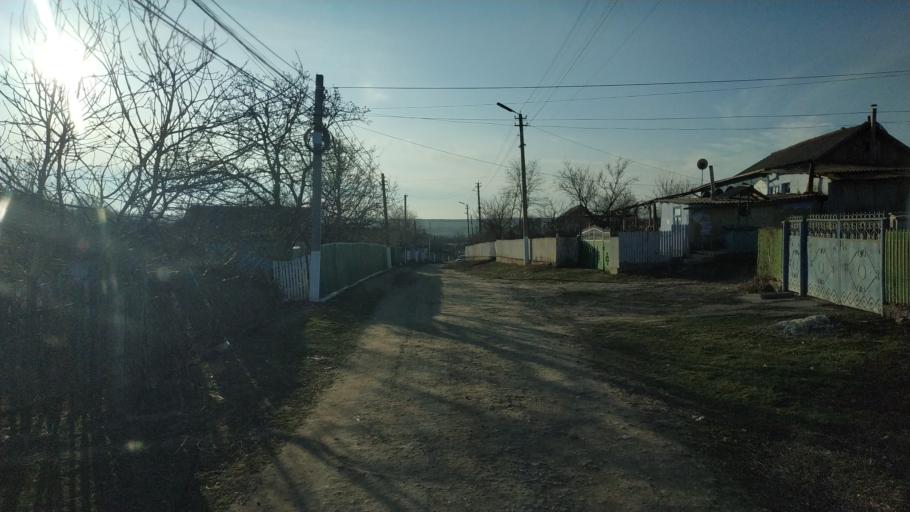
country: MD
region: Hincesti
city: Hincesti
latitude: 46.6994
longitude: 28.5369
